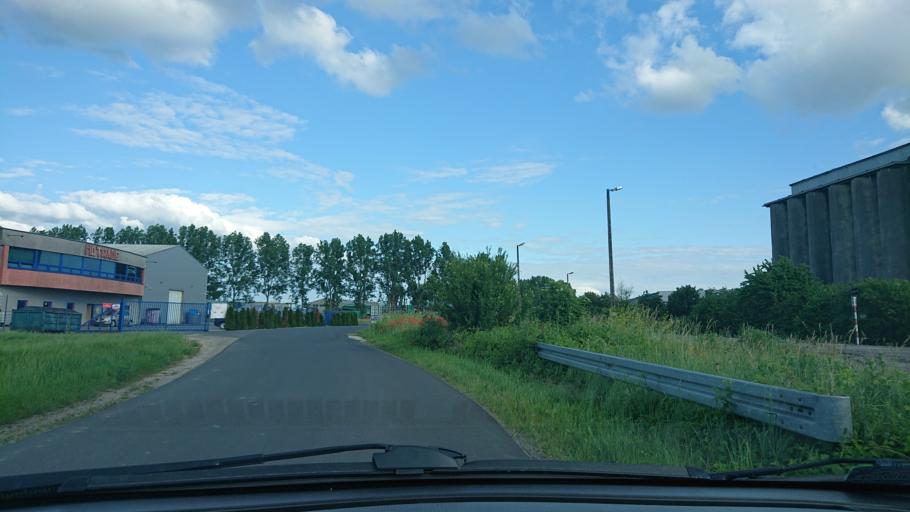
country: PL
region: Greater Poland Voivodeship
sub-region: Powiat gnieznienski
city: Gniezno
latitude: 52.5572
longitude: 17.6157
